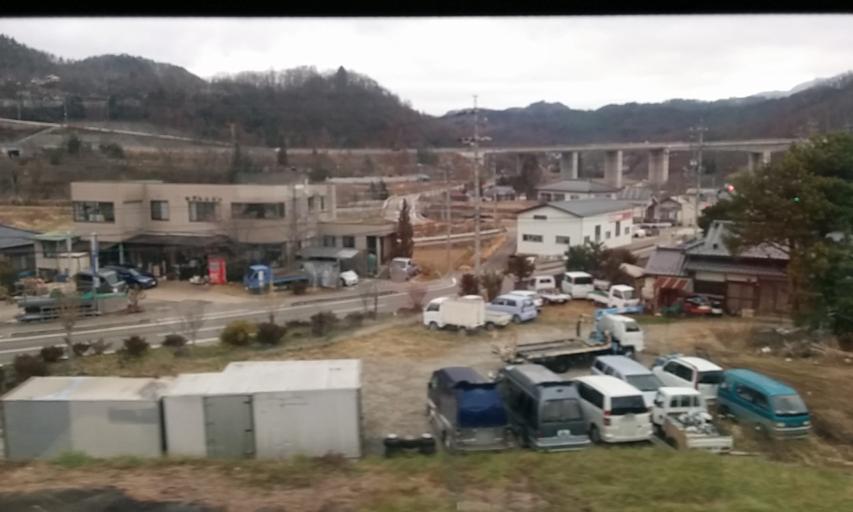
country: JP
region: Nagano
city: Hotaka
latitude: 36.4297
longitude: 138.0144
